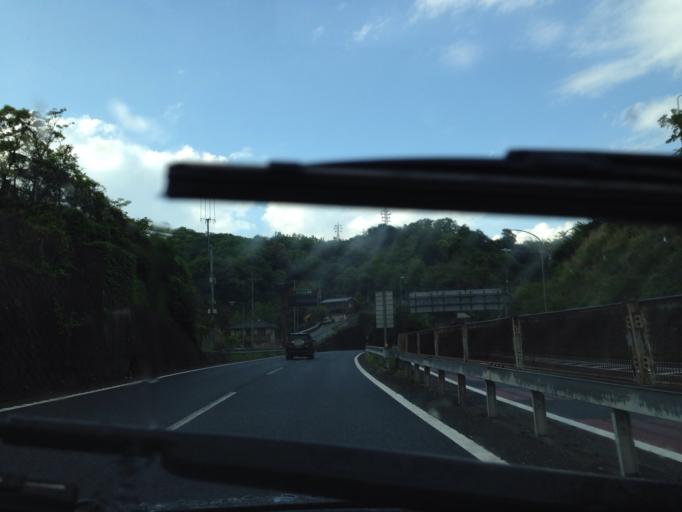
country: JP
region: Kanagawa
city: Odawara
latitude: 35.2473
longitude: 139.1327
